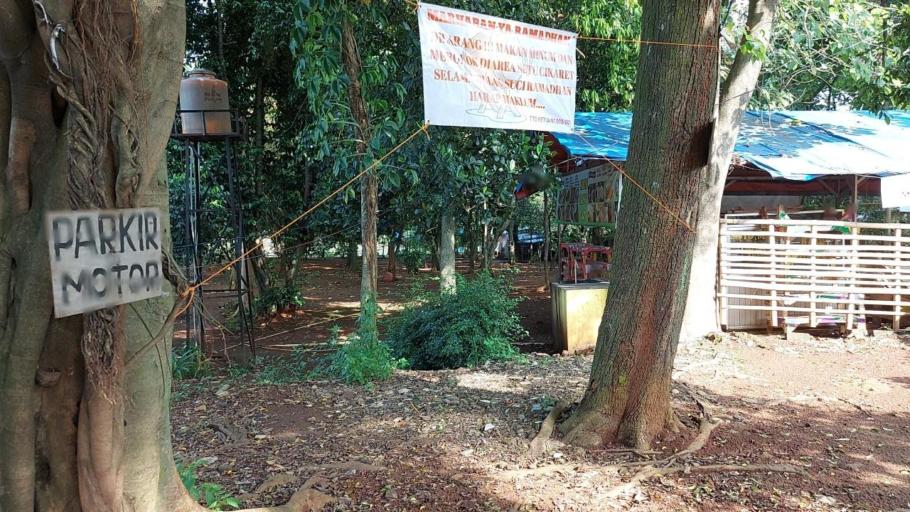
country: ID
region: West Java
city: Cibinong
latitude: -6.4677
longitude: 106.8365
